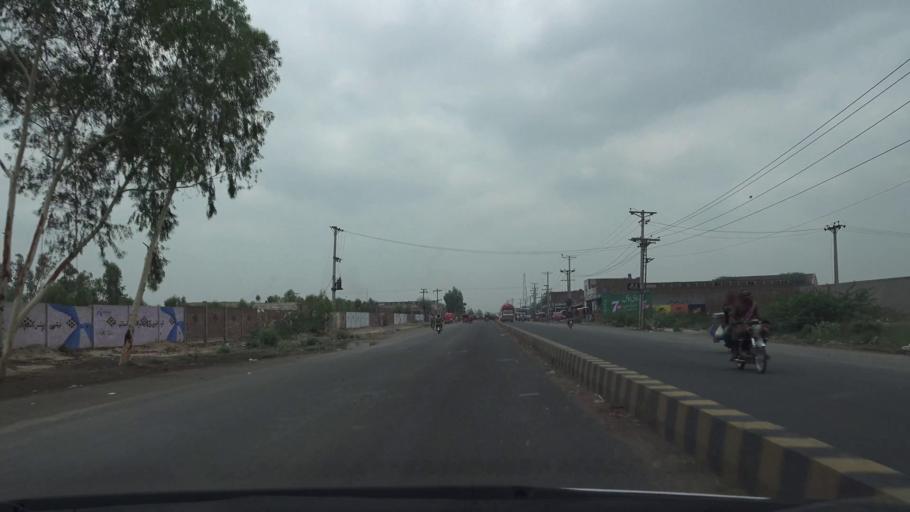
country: PK
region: Punjab
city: Faisalabad
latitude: 31.3934
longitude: 73.1799
